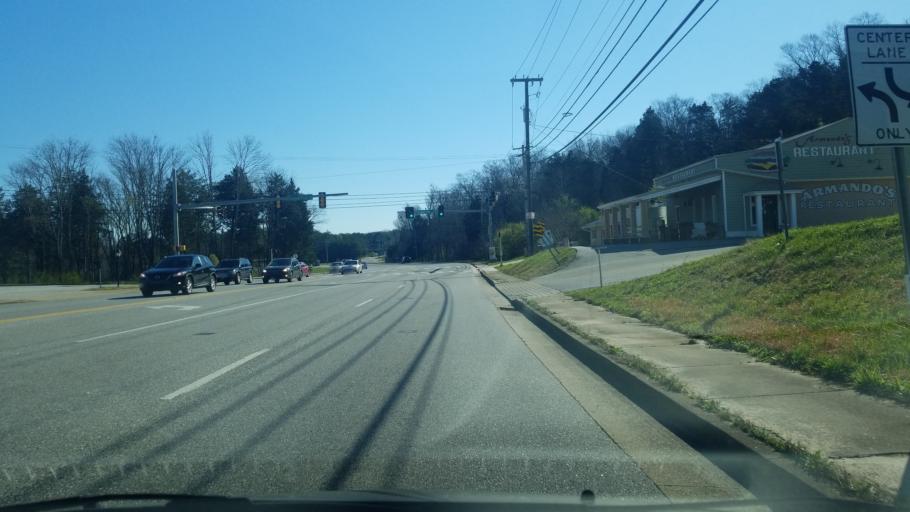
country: US
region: Tennessee
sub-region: Hamilton County
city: Middle Valley
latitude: 35.1710
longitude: -85.1772
